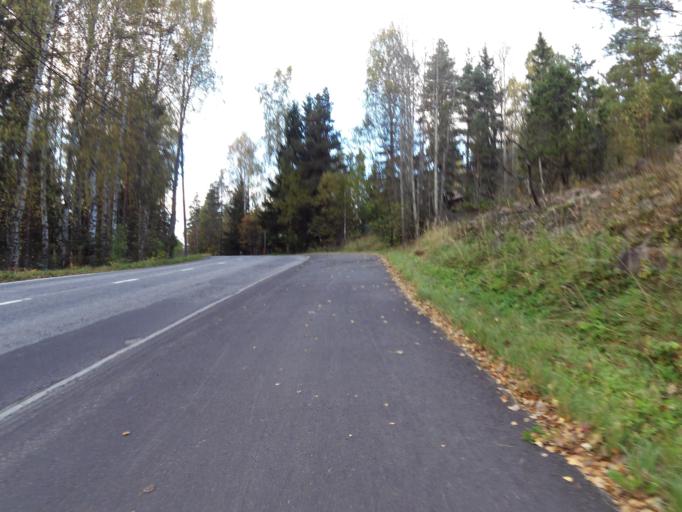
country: FI
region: Uusimaa
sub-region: Helsinki
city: Kauniainen
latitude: 60.2944
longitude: 24.7402
